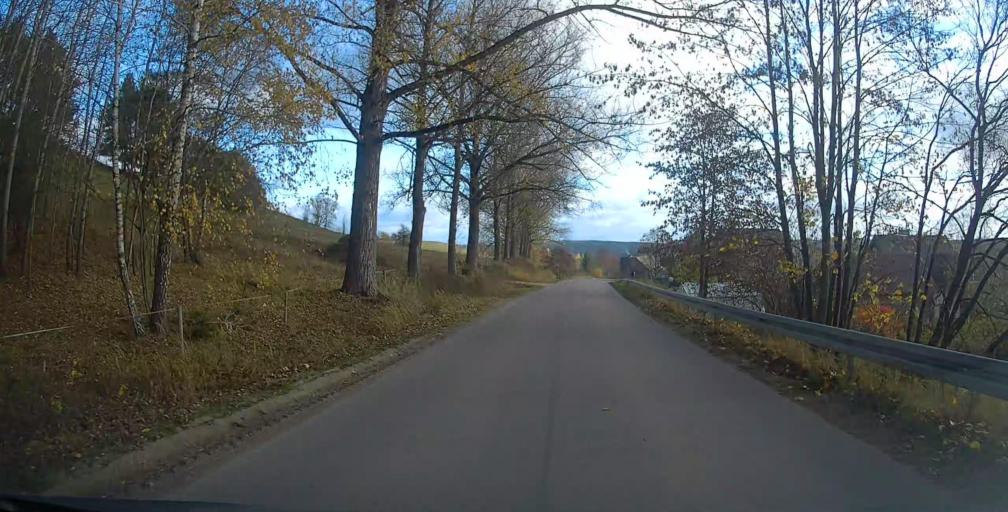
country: PL
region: Podlasie
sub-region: Suwalki
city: Suwalki
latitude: 54.2845
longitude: 22.8933
